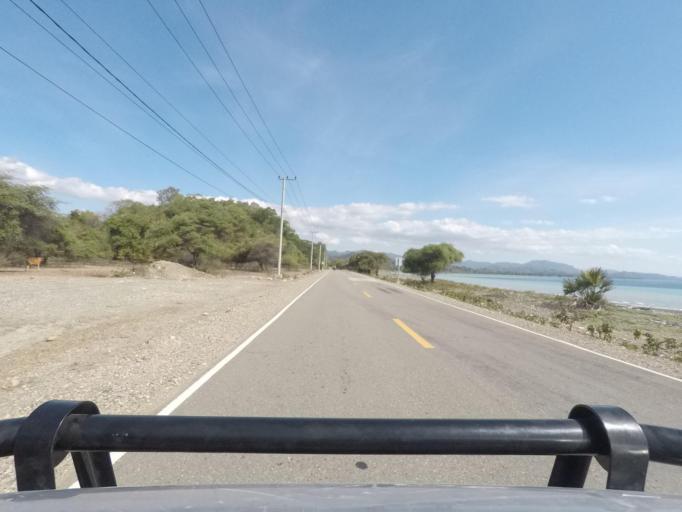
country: ID
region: East Nusa Tenggara
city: Atambua
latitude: -8.9333
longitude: 124.9804
